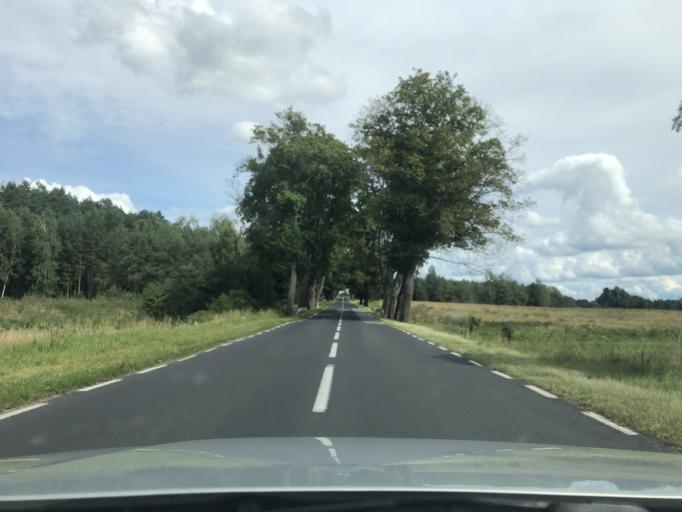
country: PL
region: Greater Poland Voivodeship
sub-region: Powiat pilski
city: Szydlowo
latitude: 53.0815
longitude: 16.6051
